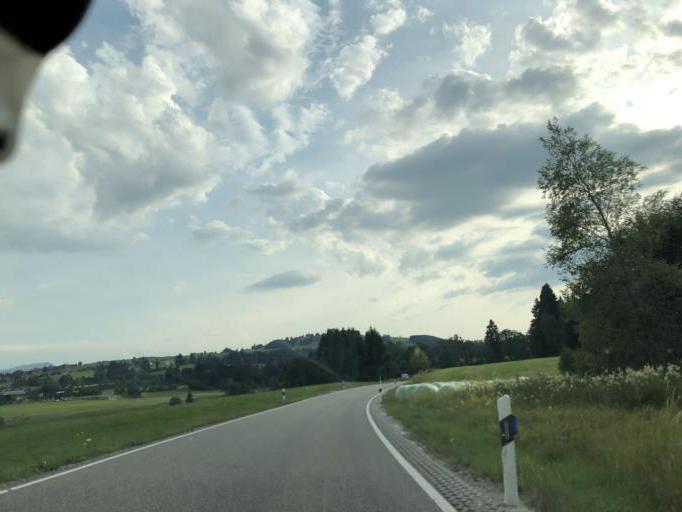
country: DE
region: Bavaria
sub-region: Swabia
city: Oy-Mittelberg
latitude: 47.6612
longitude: 10.4608
